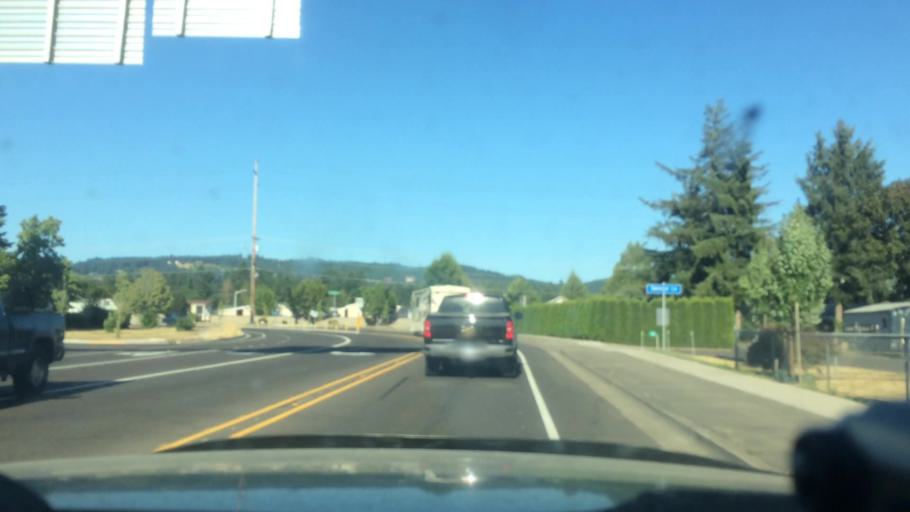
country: US
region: Oregon
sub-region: Yamhill County
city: Newberg
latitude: 45.2937
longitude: -122.9486
